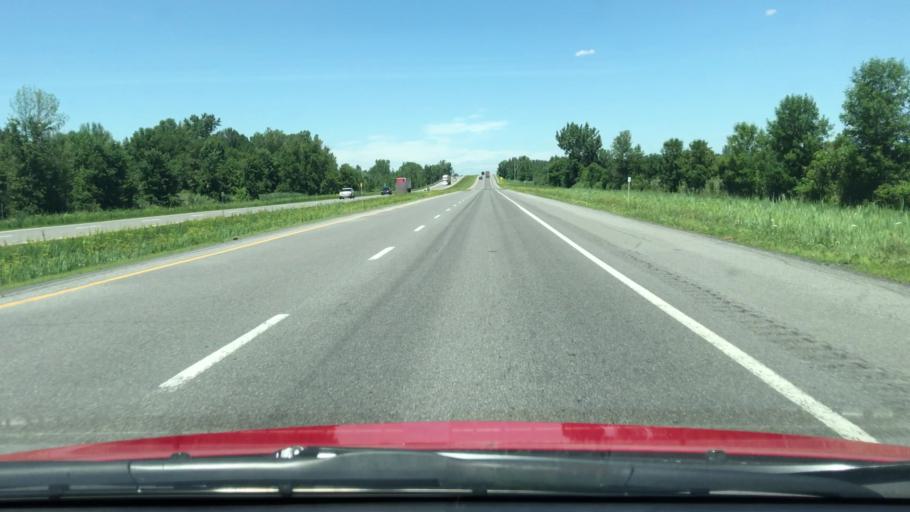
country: CA
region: Quebec
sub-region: Monteregie
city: Napierville
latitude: 45.2316
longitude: -73.4748
